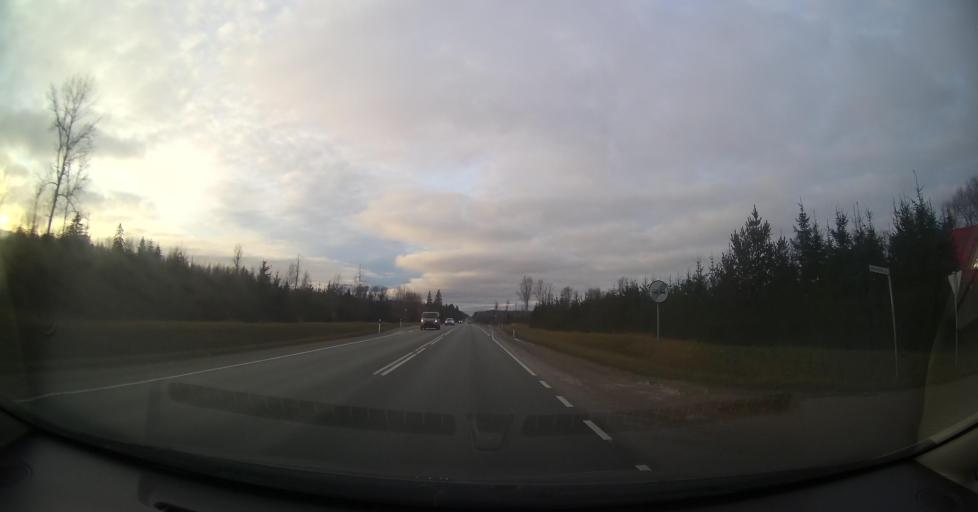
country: EE
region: Tartu
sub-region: Tartu linn
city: Tartu
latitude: 58.4085
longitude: 26.6110
